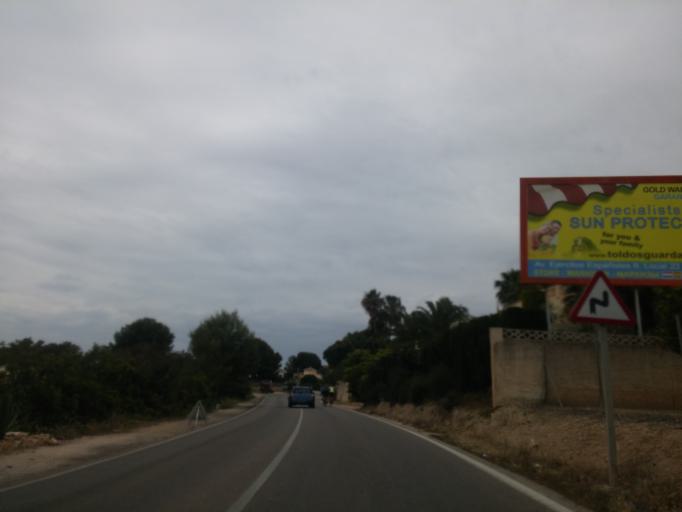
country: ES
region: Valencia
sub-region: Provincia de Alicante
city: Calp
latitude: 38.6599
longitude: 0.0813
